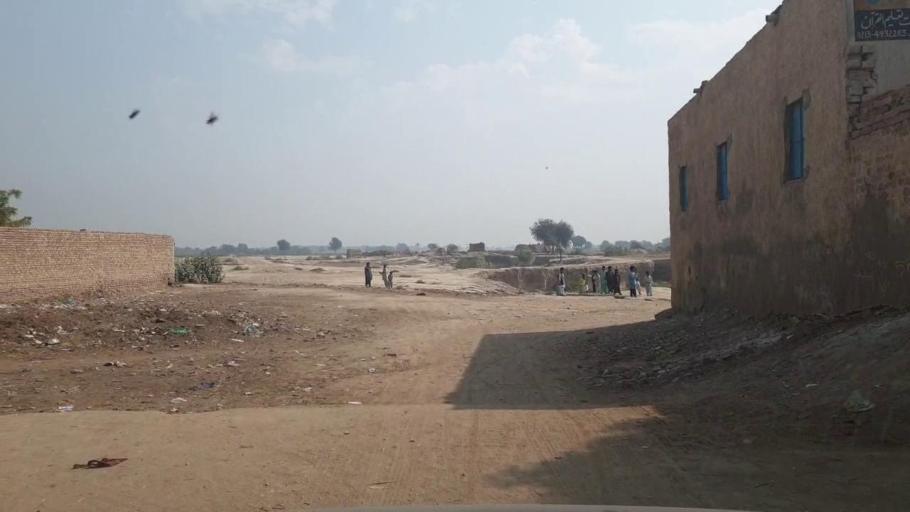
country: PK
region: Sindh
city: Hala
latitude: 25.7930
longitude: 68.4227
